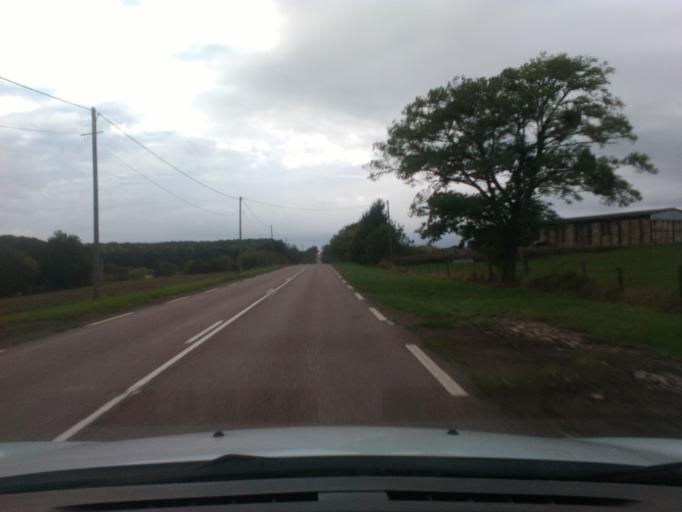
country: FR
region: Lorraine
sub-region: Departement des Vosges
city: Chatel-sur-Moselle
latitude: 48.3489
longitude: 6.4230
